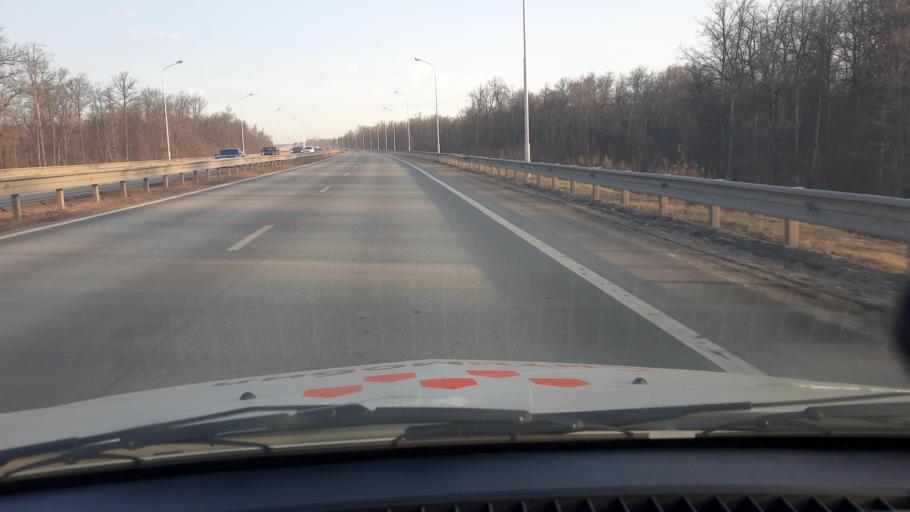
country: RU
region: Bashkortostan
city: Ufa
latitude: 54.6750
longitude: 56.0228
